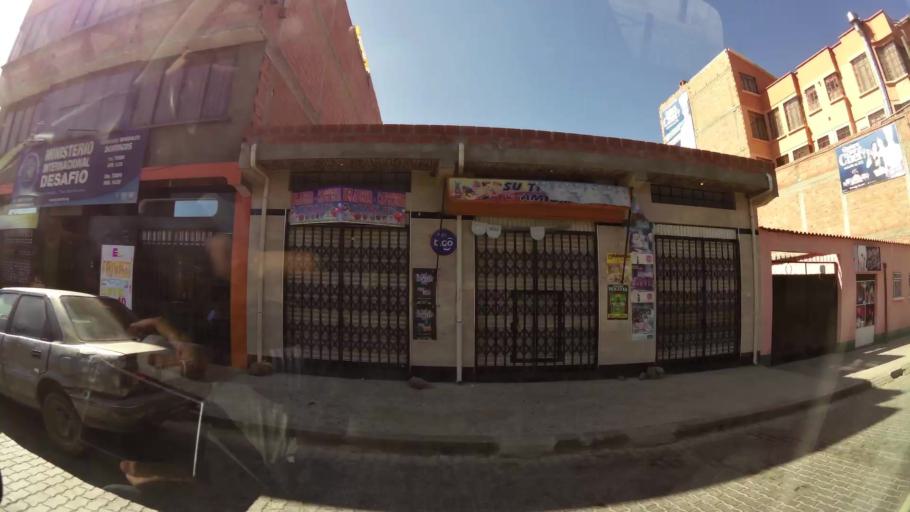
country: BO
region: La Paz
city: La Paz
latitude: -16.5217
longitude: -68.1527
